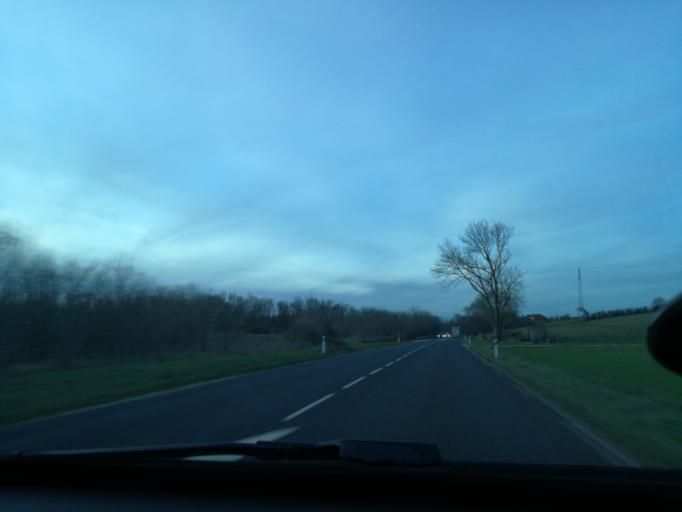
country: FR
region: Lorraine
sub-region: Departement de la Meuse
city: Fains-Veel
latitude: 48.8026
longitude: 5.1173
